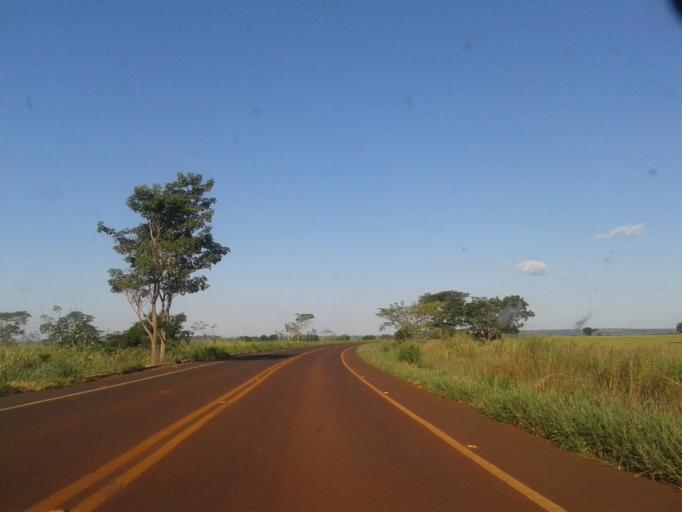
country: BR
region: Minas Gerais
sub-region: Santa Vitoria
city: Santa Vitoria
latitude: -18.6913
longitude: -49.8881
